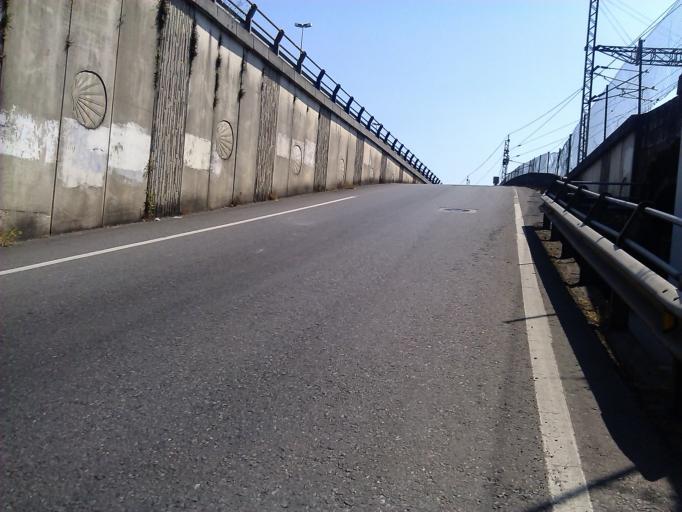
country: ES
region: Galicia
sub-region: Provincia da Coruna
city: Santiago de Compostela
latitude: 42.8730
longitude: -8.5390
